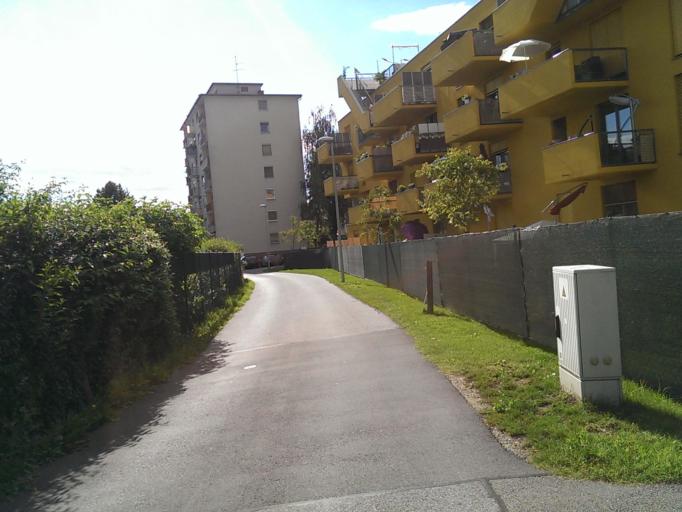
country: AT
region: Styria
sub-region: Graz Stadt
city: Graz
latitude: 47.0535
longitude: 15.4528
